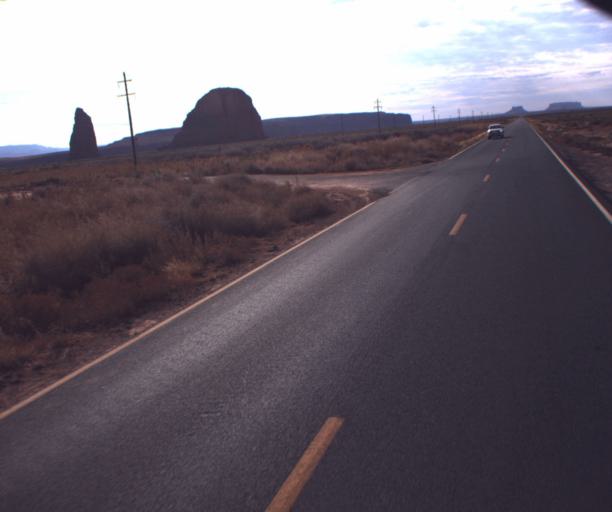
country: US
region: Arizona
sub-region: Apache County
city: Many Farms
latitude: 36.6745
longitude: -109.6006
